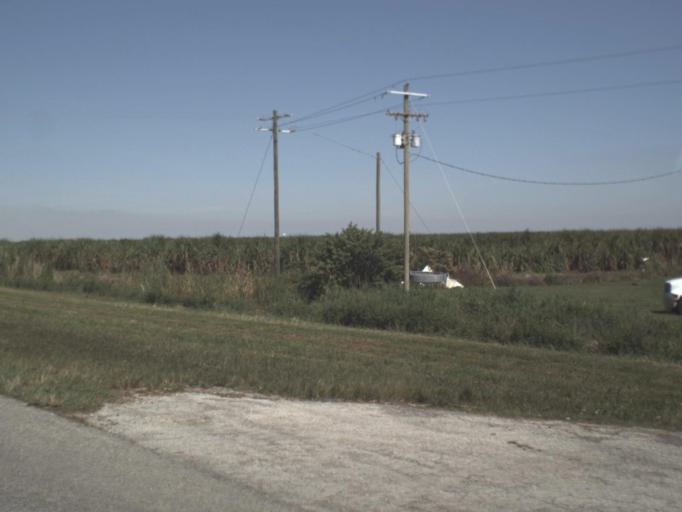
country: US
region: Florida
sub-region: Glades County
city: Moore Haven
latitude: 26.7824
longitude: -81.0827
